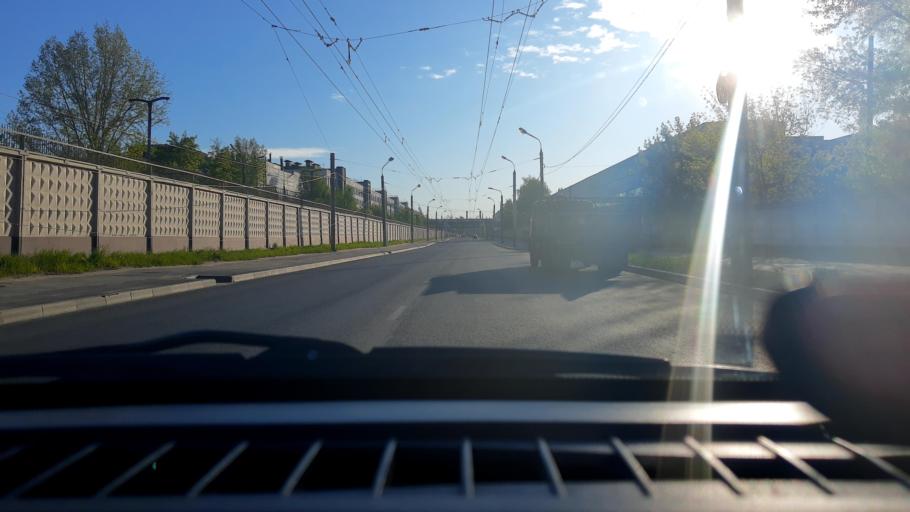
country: RU
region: Nizjnij Novgorod
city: Nizhniy Novgorod
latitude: 56.2463
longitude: 43.9057
